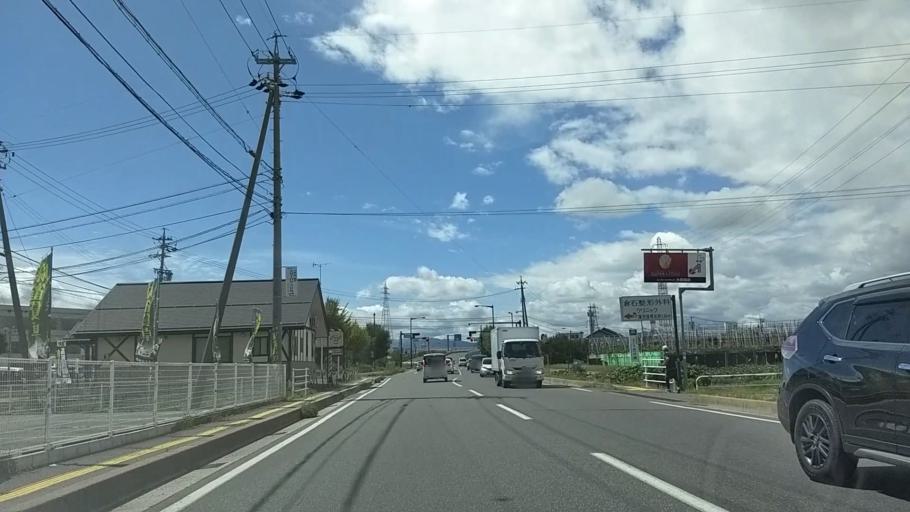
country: JP
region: Nagano
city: Nagano-shi
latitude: 36.6267
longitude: 138.2344
